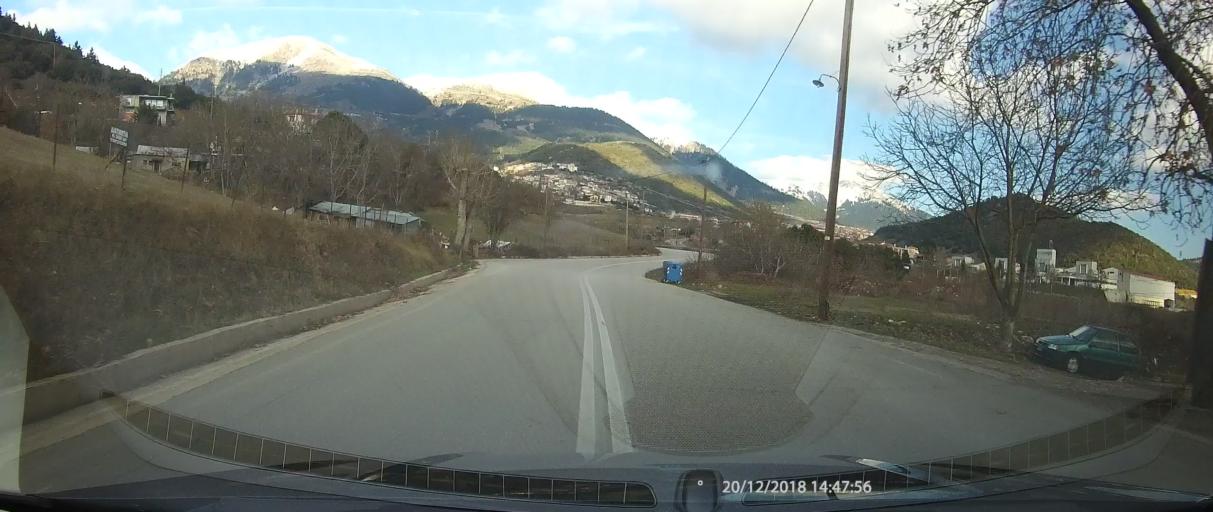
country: GR
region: Central Greece
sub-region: Nomos Evrytanias
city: Karpenisi
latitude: 38.9040
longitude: 21.7858
